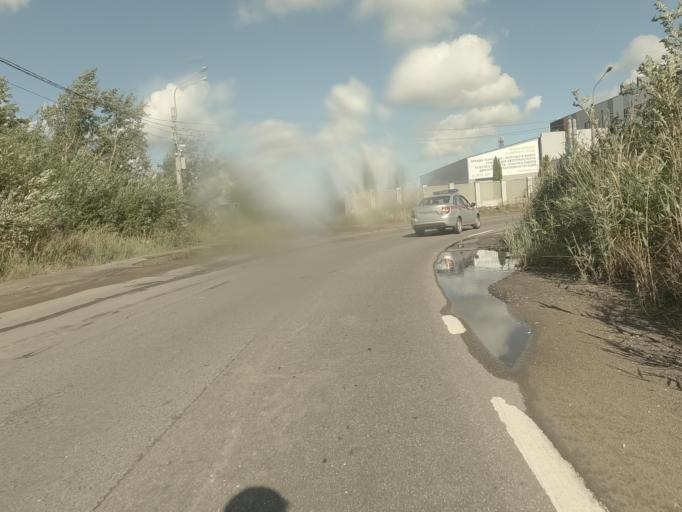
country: RU
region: St.-Petersburg
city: Krasnogvargeisky
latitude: 59.9743
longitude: 30.5263
